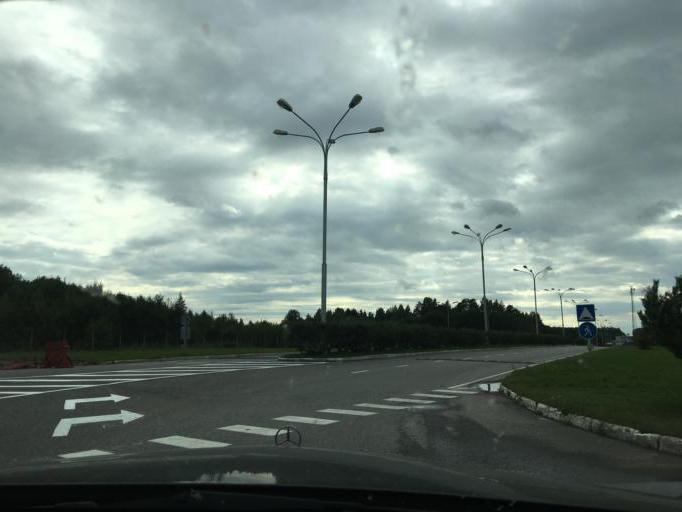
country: RU
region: Pskov
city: Pechory
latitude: 57.6445
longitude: 27.3865
